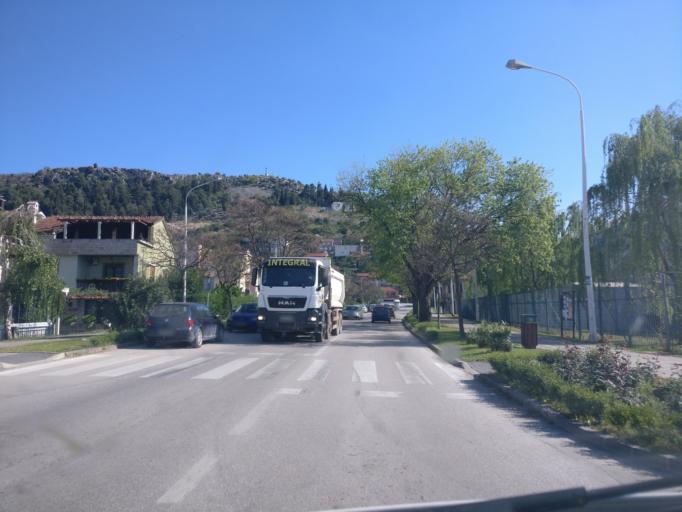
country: BA
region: Federation of Bosnia and Herzegovina
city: Capljina
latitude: 43.1134
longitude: 17.7006
